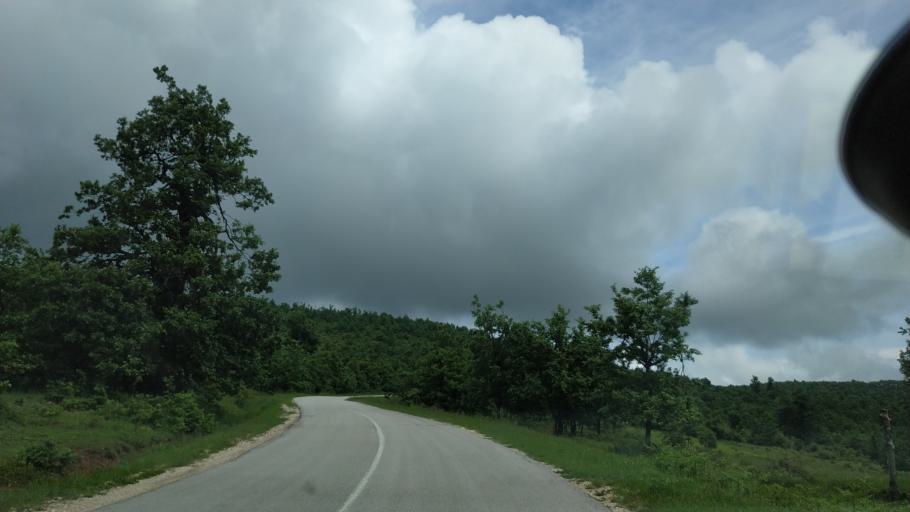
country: RS
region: Central Serbia
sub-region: Zajecarski Okrug
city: Soko Banja
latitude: 43.7147
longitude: 21.9406
